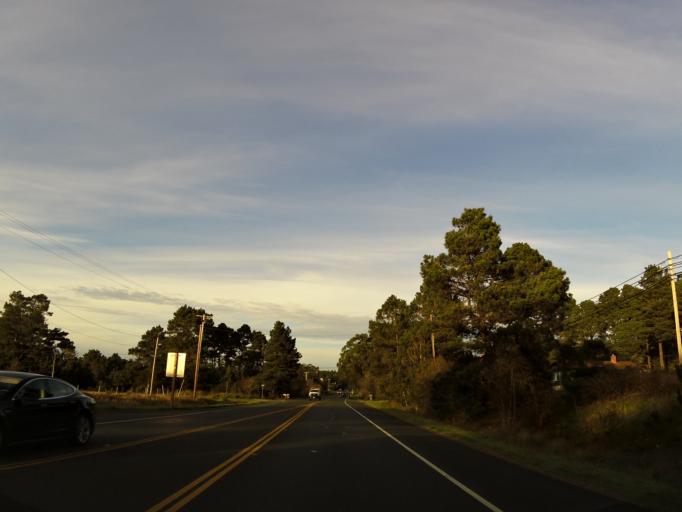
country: US
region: California
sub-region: Mendocino County
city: Fort Bragg
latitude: 39.3849
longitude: -123.8134
